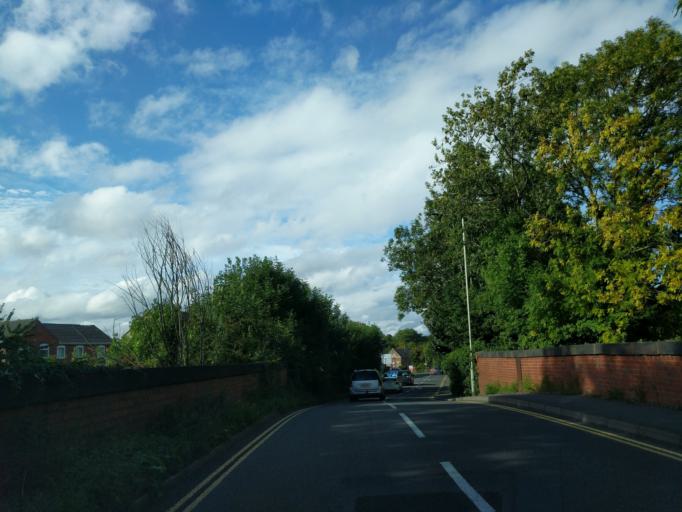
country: GB
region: England
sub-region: Leicestershire
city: Coalville
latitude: 52.7052
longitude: -1.3724
